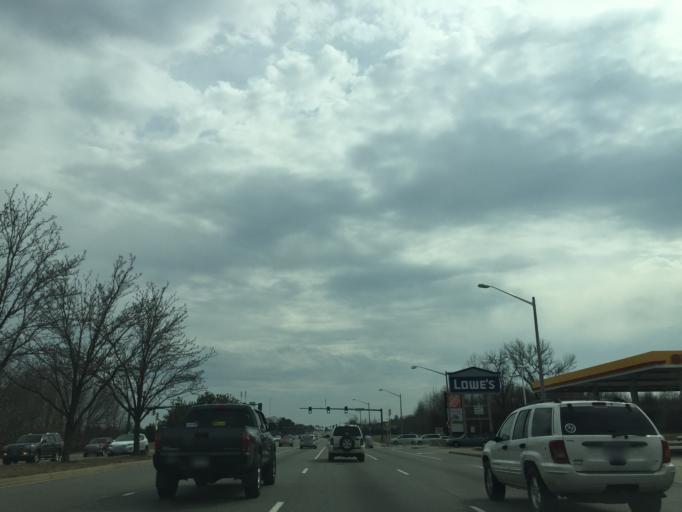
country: US
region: Virginia
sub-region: York County
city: Yorktown
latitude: 37.1245
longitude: -76.5092
